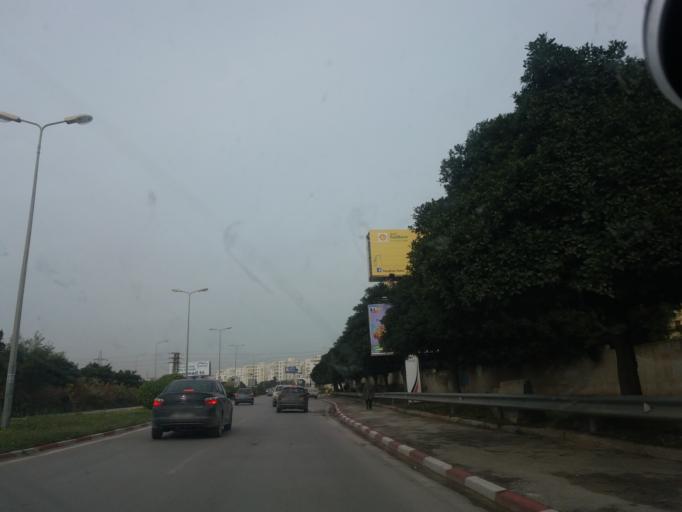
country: TN
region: Tunis
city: Tunis
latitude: 36.8497
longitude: 10.1563
